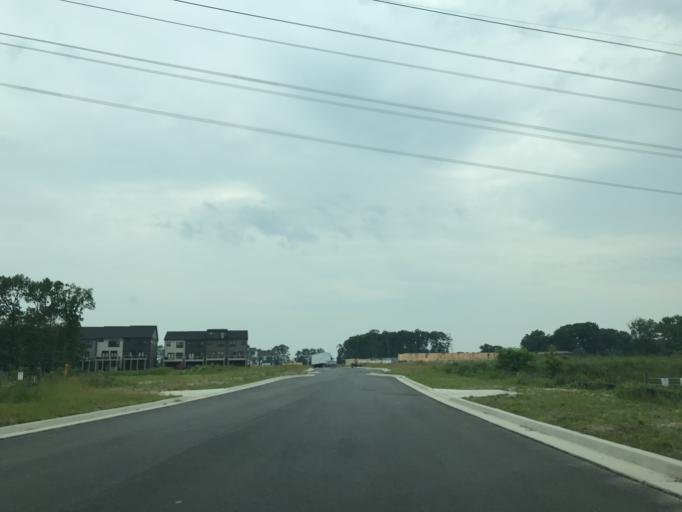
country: US
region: Maryland
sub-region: Baltimore County
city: Bowleys Quarters
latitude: 39.3562
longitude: -76.4023
